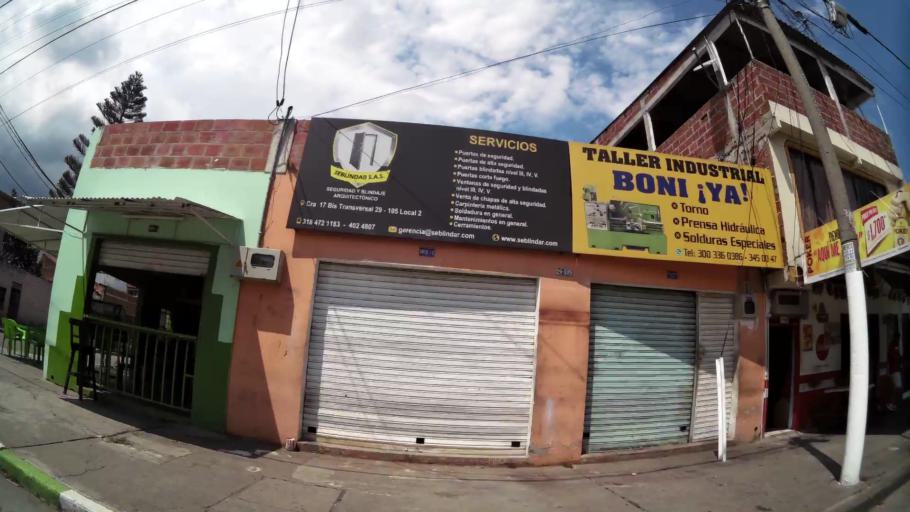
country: CO
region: Valle del Cauca
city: Cali
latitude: 3.4430
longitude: -76.5162
